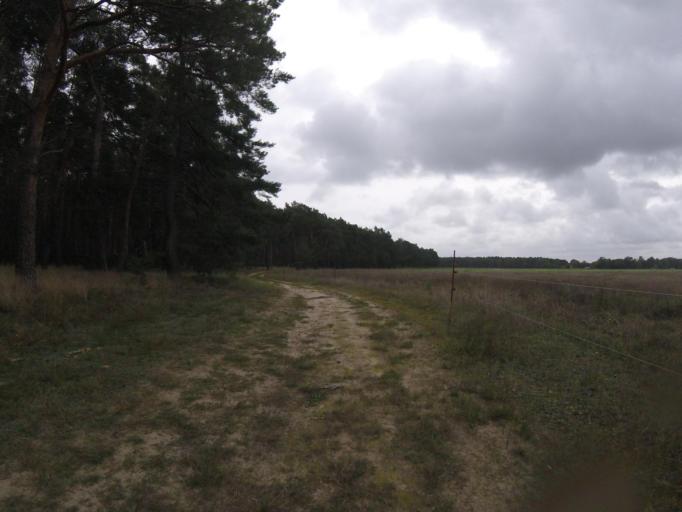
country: DE
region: Brandenburg
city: Gross Koris
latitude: 52.1852
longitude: 13.6727
